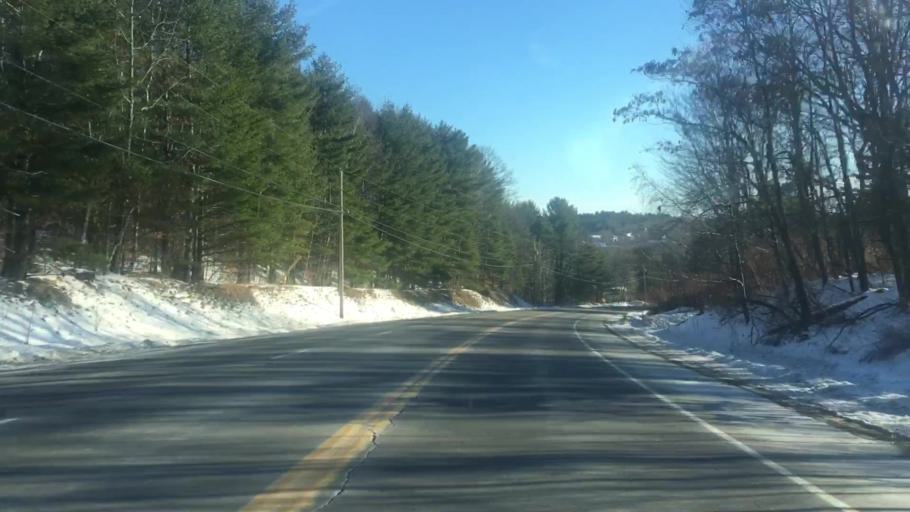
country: US
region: Maine
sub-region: Somerset County
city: Norridgewock
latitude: 44.7211
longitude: -69.7987
